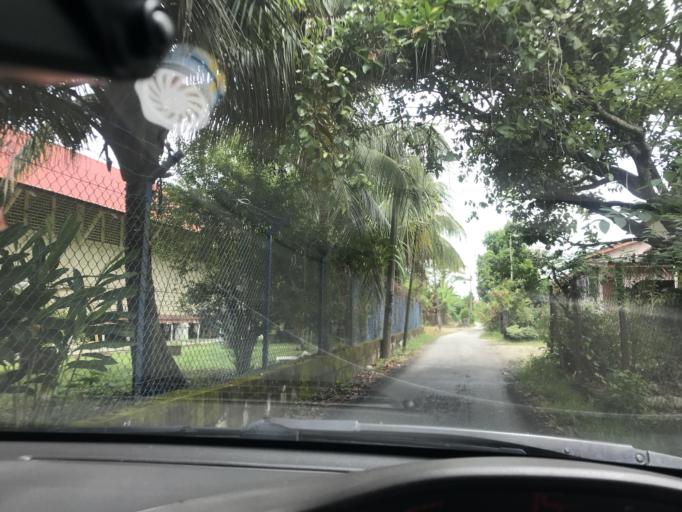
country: MY
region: Kelantan
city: Kota Bharu
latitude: 6.1192
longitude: 102.2212
